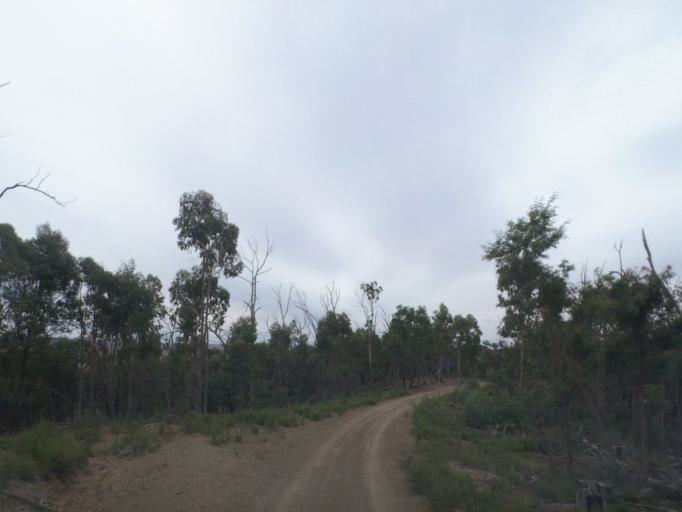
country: AU
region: Victoria
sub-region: Murrindindi
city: Alexandra
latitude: -37.3741
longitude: 145.5580
